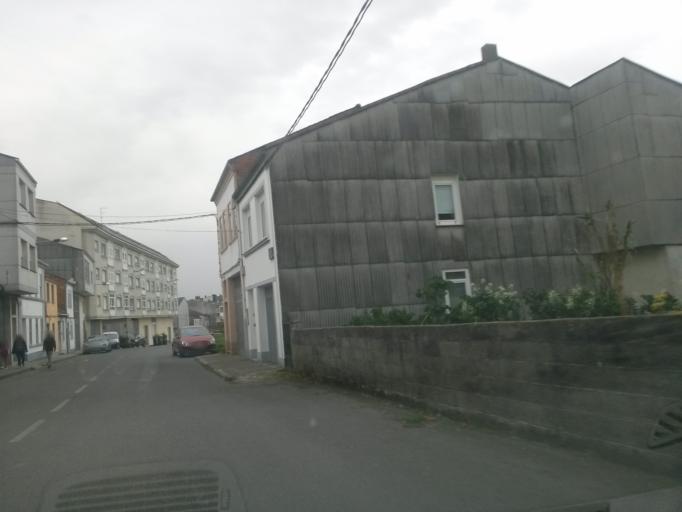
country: ES
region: Galicia
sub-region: Provincia de Lugo
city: Lugo
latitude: 43.0284
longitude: -7.5649
